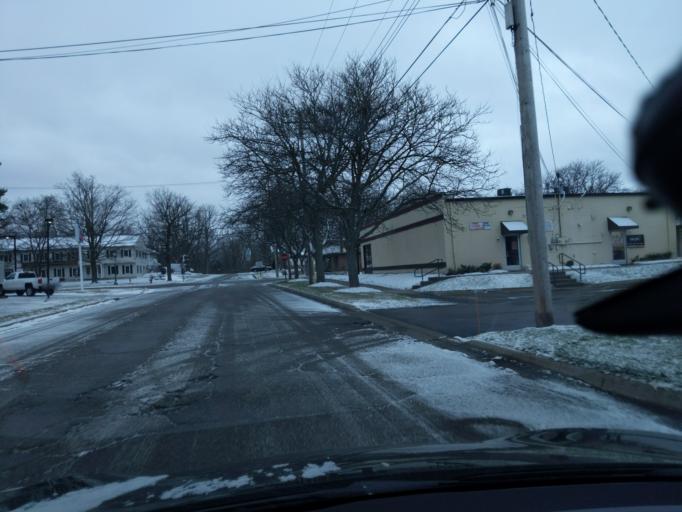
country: US
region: Michigan
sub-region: Ingham County
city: Okemos
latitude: 42.7171
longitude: -84.4278
